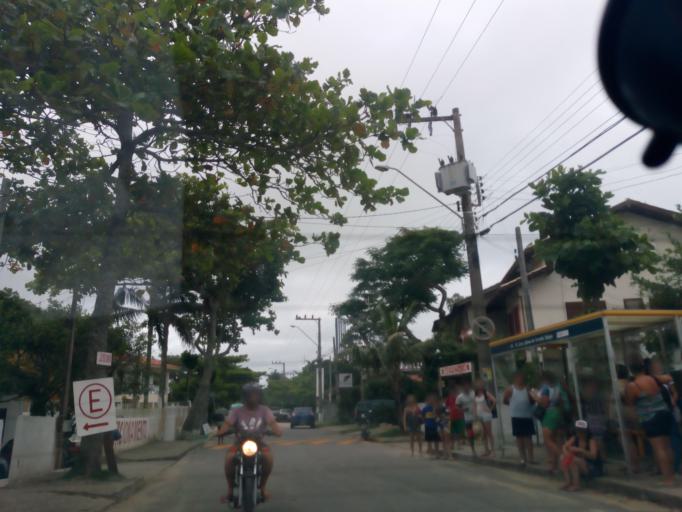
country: BR
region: Santa Catarina
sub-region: Florianopolis
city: Itacorubi
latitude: -27.3899
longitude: -48.4218
